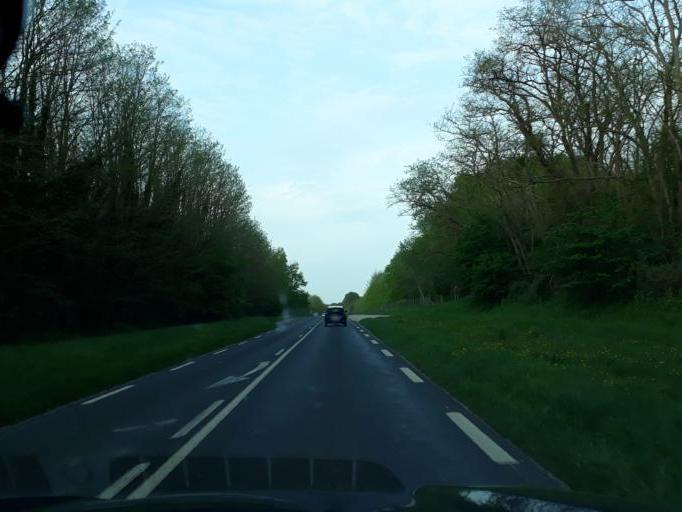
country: FR
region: Centre
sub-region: Departement du Loir-et-Cher
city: Saint-Laurent-Nouan
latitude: 47.7250
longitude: 1.6310
